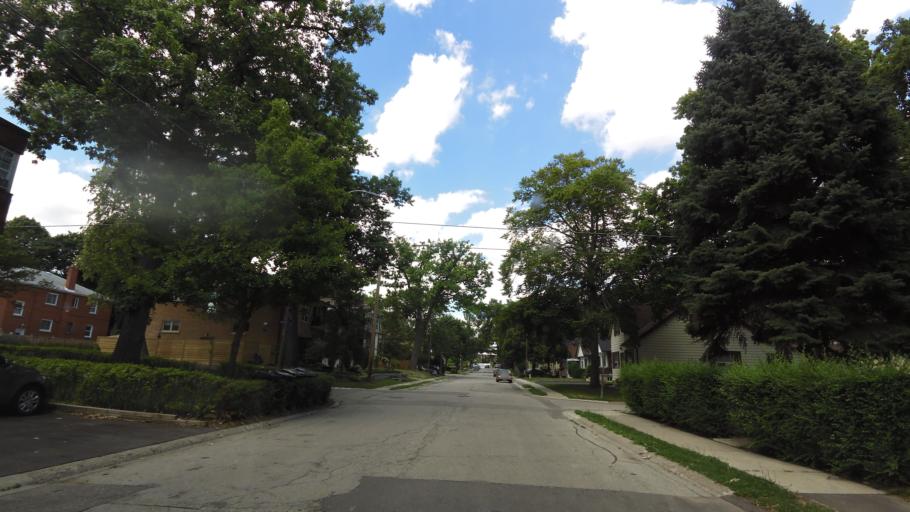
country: CA
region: Ontario
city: Etobicoke
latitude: 43.5917
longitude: -79.5346
